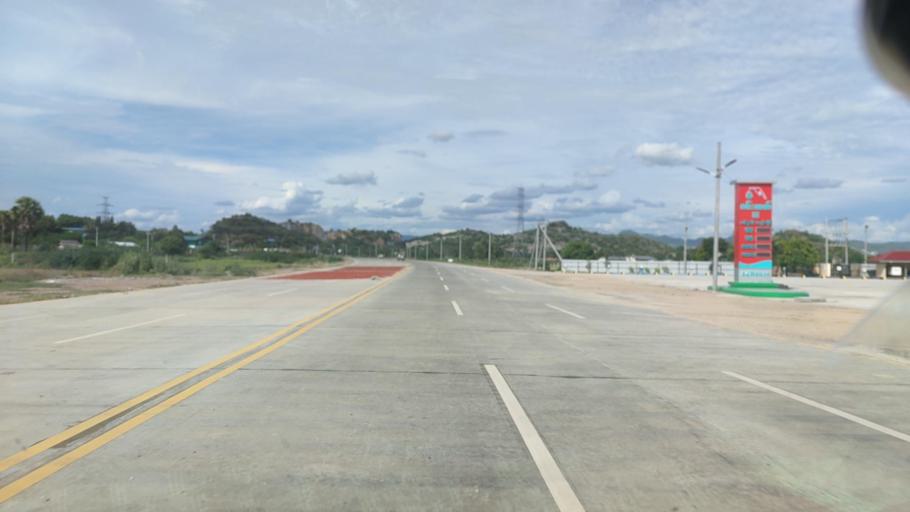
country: MM
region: Mandalay
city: Kyaukse
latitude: 21.6016
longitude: 96.1827
